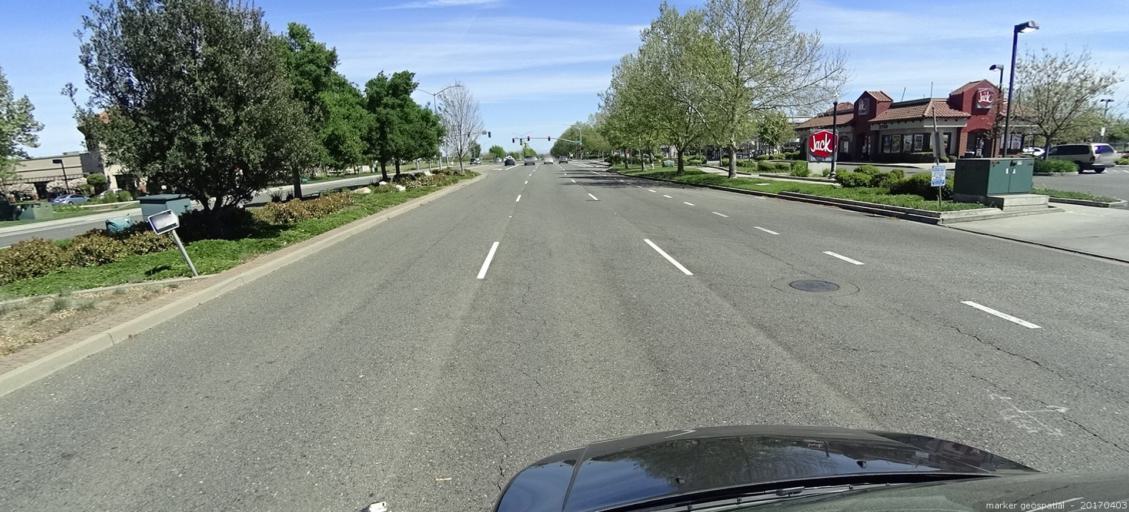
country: US
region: California
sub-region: Yolo County
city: West Sacramento
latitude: 38.6558
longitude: -121.5238
